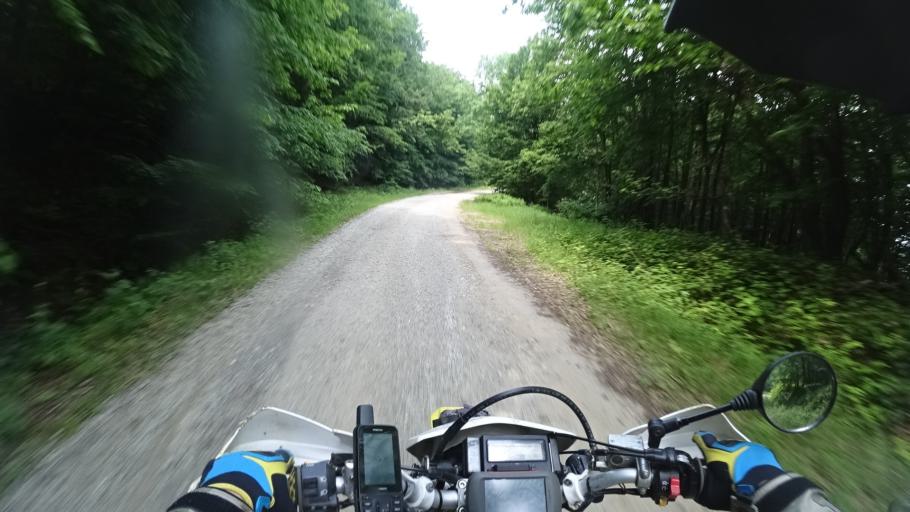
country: HR
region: Sisacko-Moslavacka
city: Gvozd
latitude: 45.3122
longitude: 15.8105
